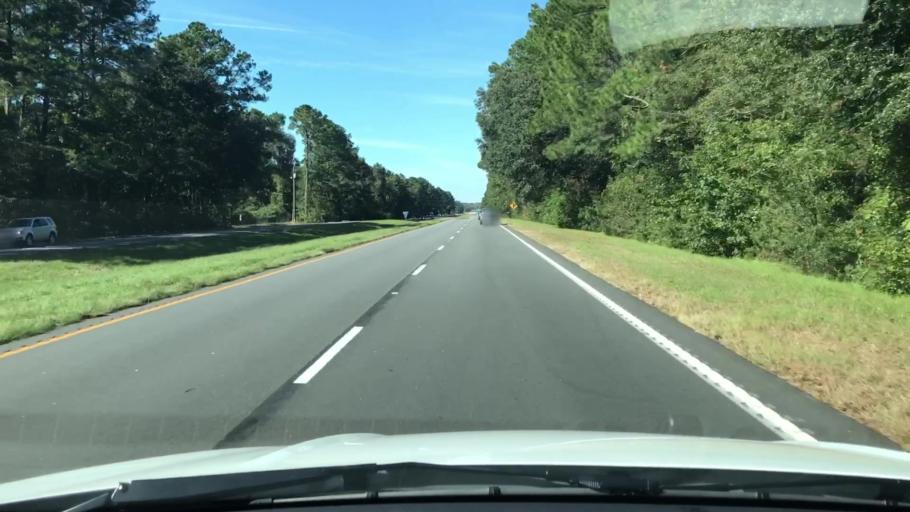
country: US
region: South Carolina
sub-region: Beaufort County
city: Laurel Bay
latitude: 32.5886
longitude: -80.7461
